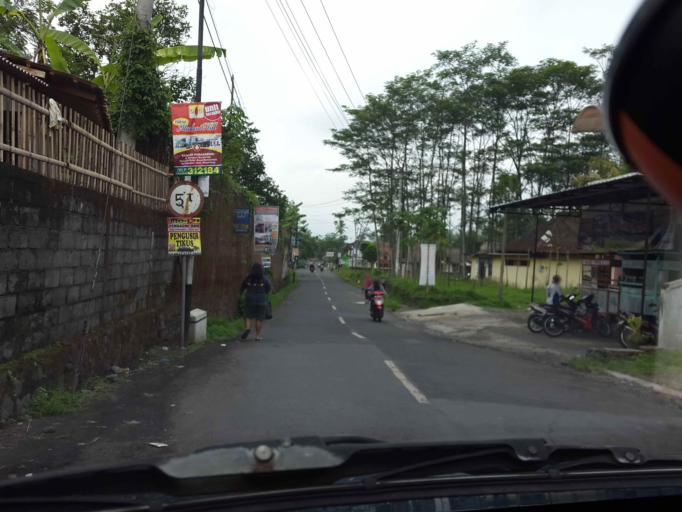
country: ID
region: Central Java
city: Mertoyudan
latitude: -7.5301
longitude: 110.2307
